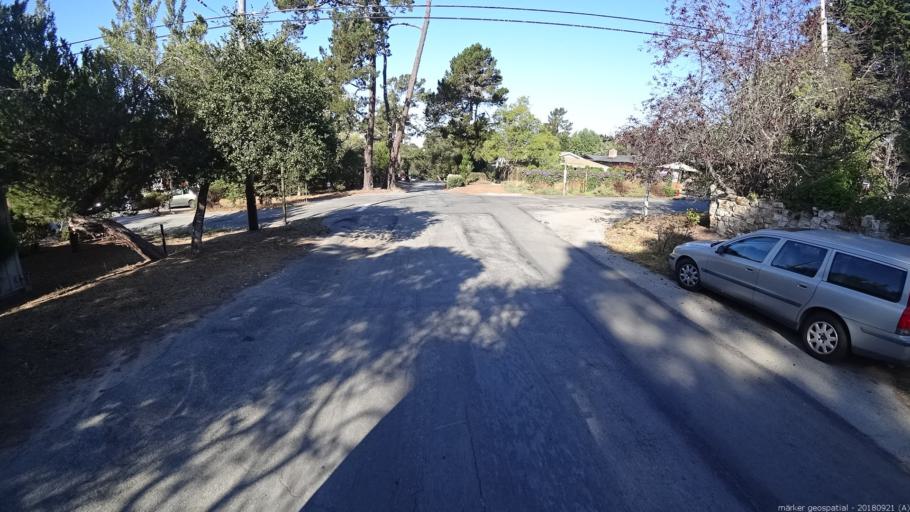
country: US
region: California
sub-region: Monterey County
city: Carmel-by-the-Sea
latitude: 36.5618
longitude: -121.9163
